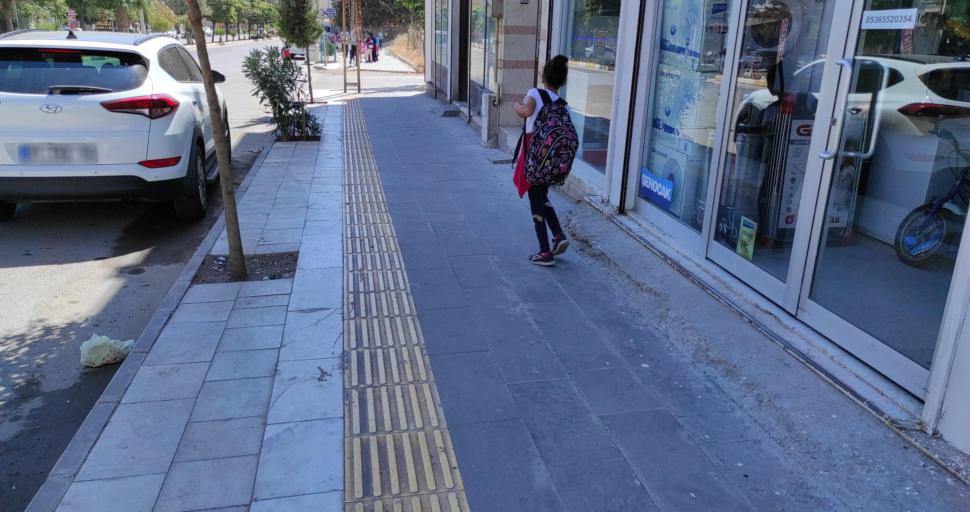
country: TR
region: Kilis
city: Kilis
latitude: 36.7239
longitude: 37.1046
